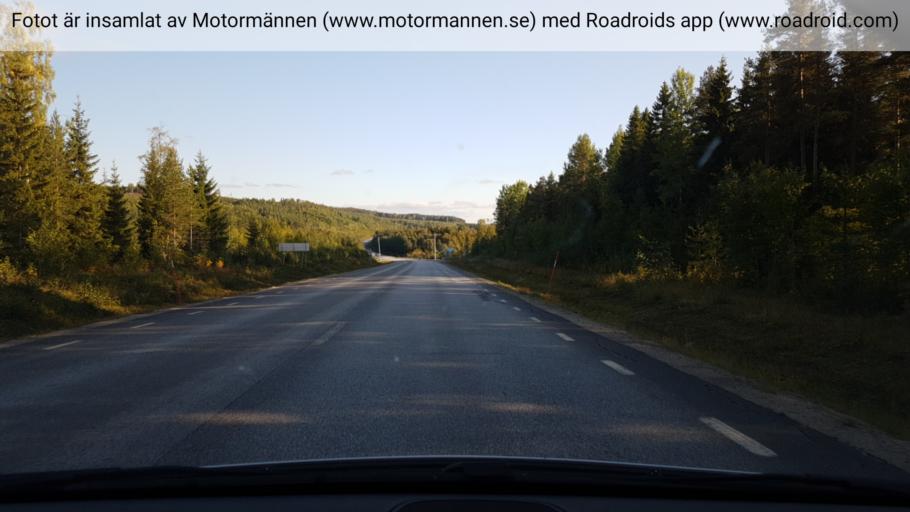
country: SE
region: Vaesterbotten
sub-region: Vannas Kommun
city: Vaennaes
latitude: 64.0005
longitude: 19.7233
